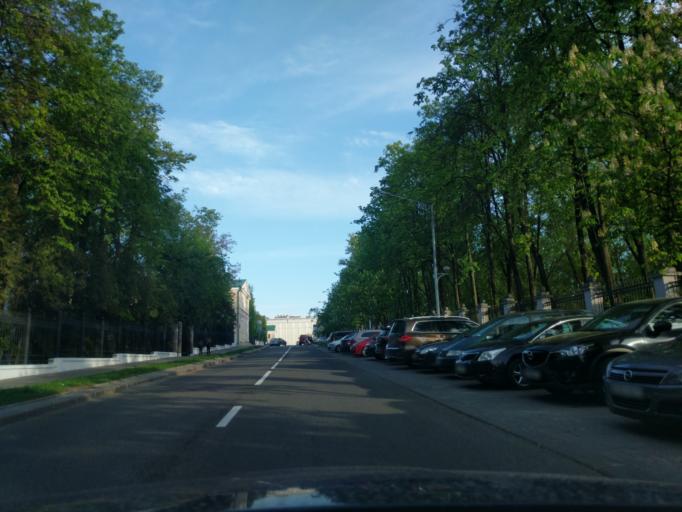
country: BY
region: Minsk
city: Minsk
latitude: 53.9045
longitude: 27.5760
